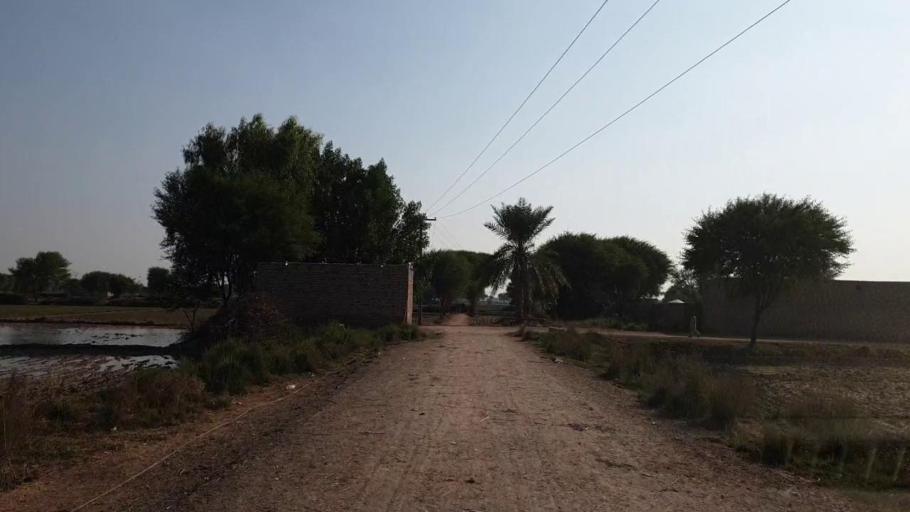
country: PK
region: Sindh
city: Sehwan
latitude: 26.4378
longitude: 67.8114
